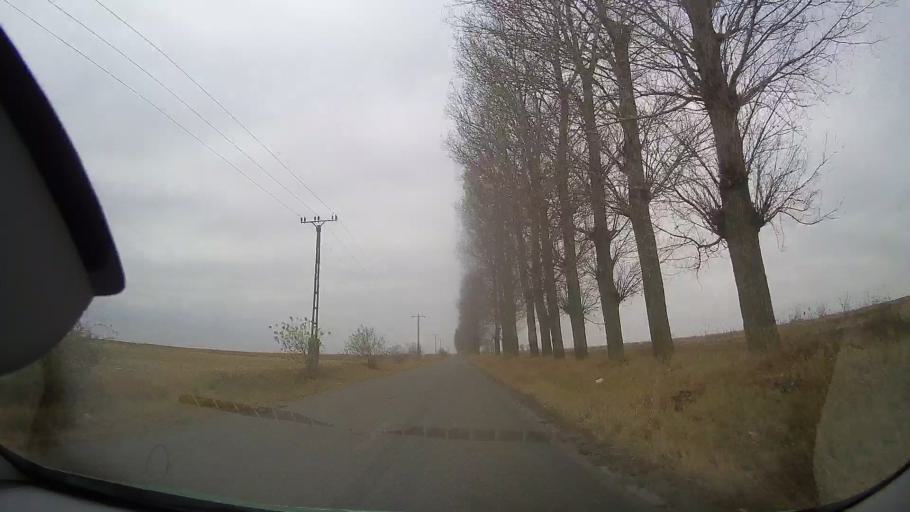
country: RO
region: Buzau
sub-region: Comuna Pogoanele
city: Pogoanele
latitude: 44.9596
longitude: 27.0200
